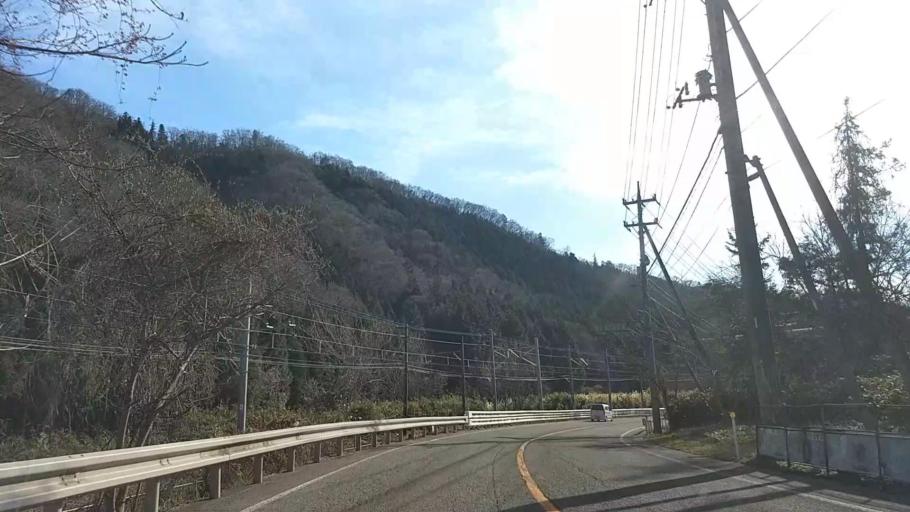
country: JP
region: Yamanashi
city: Otsuki
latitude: 35.5836
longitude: 138.9382
